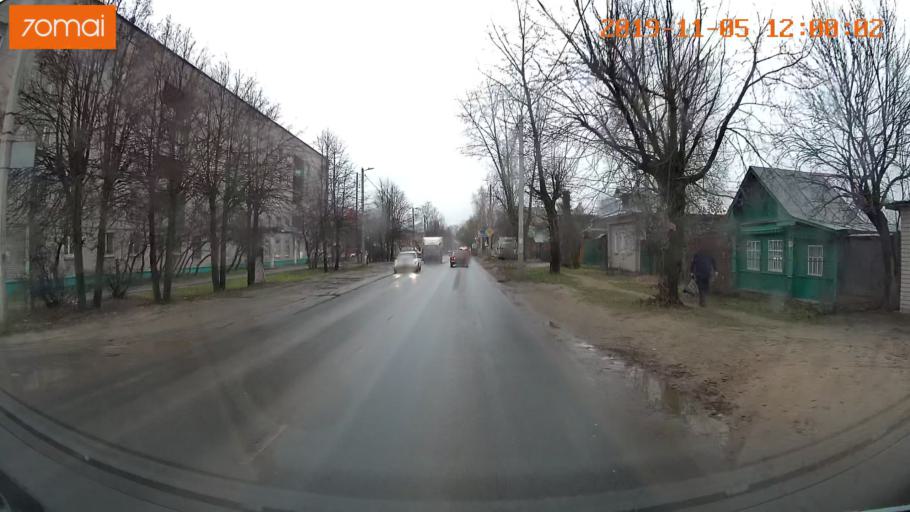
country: RU
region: Ivanovo
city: Kokhma
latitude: 56.9765
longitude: 41.0488
